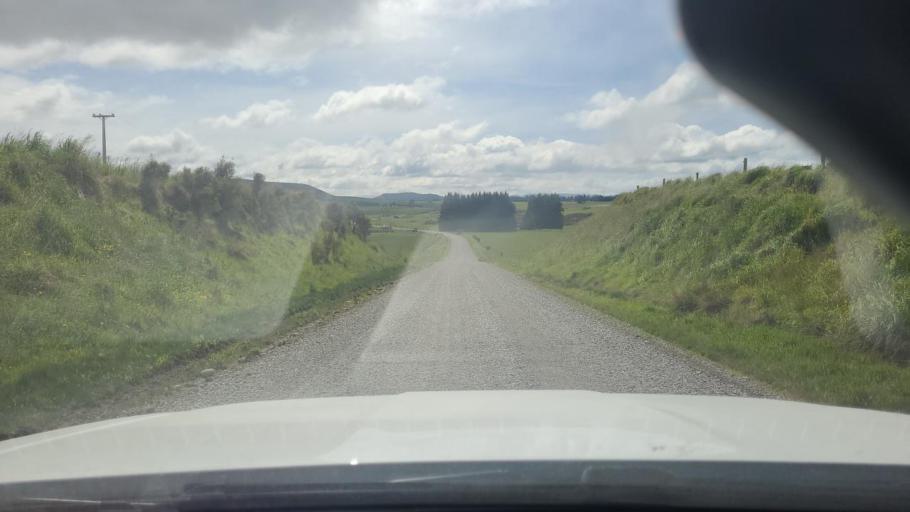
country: NZ
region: Southland
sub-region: Southland District
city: Te Anau
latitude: -45.4853
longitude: 167.8974
